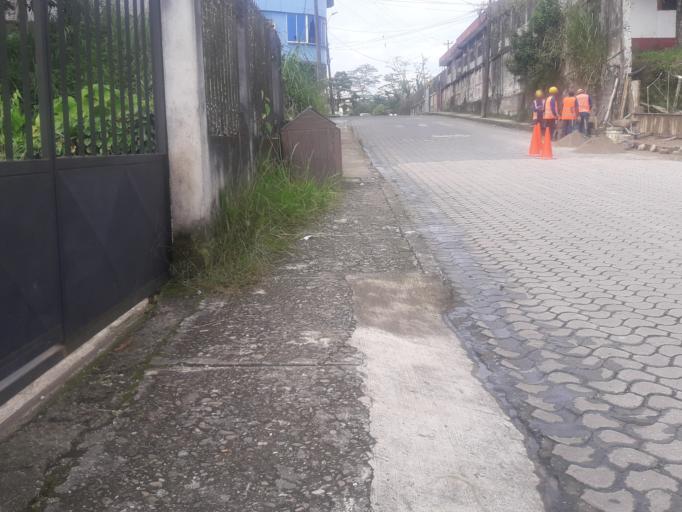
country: EC
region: Napo
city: Tena
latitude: -0.9954
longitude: -77.8112
